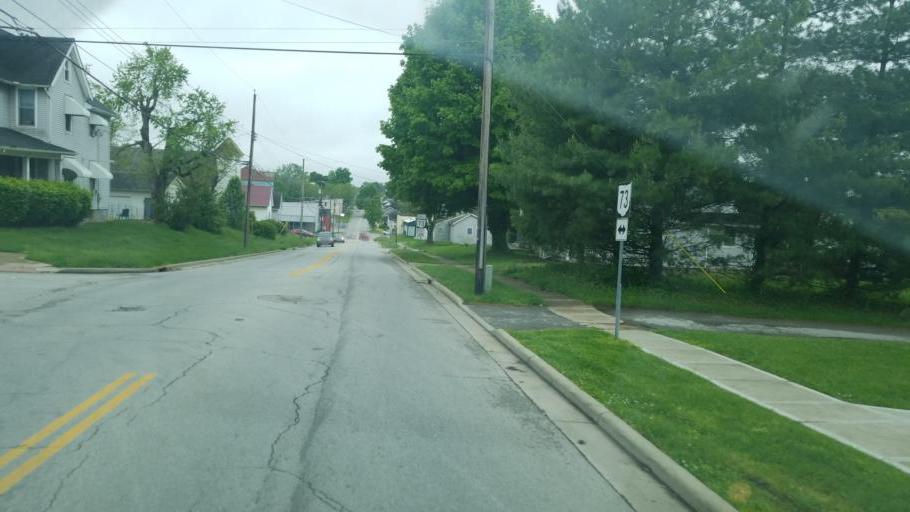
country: US
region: Ohio
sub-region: Highland County
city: Hillsboro
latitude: 39.2091
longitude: -83.6124
